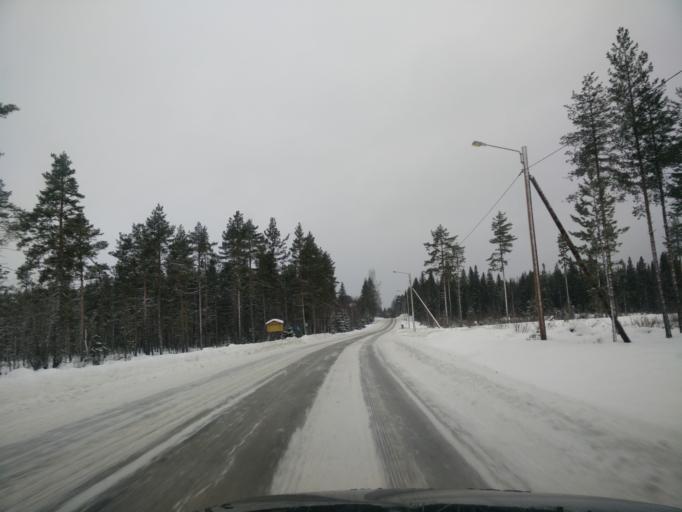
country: SE
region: Jaemtland
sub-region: Braecke Kommun
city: Braecke
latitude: 62.3954
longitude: 15.2215
